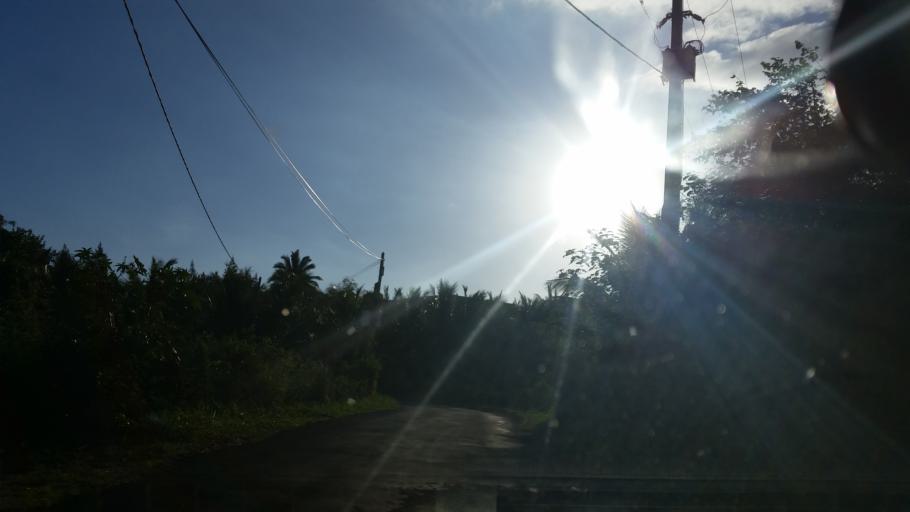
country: RE
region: Reunion
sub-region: Reunion
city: Saint-Joseph
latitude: -21.3780
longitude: 55.6707
